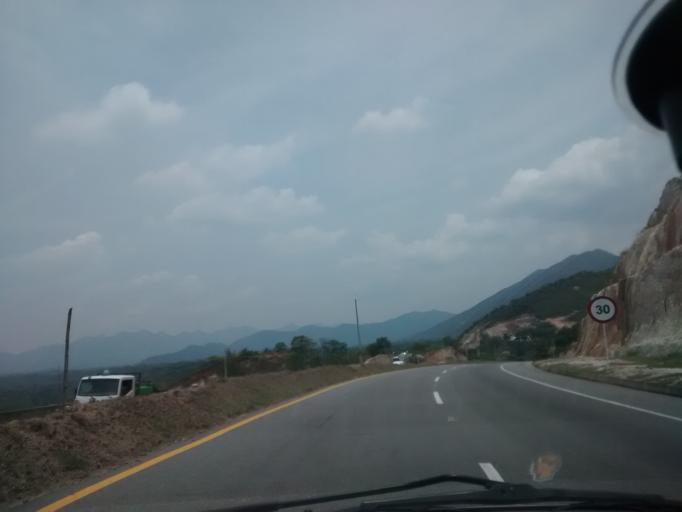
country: CO
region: Tolima
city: Espinal
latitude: 4.2229
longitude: -74.9757
